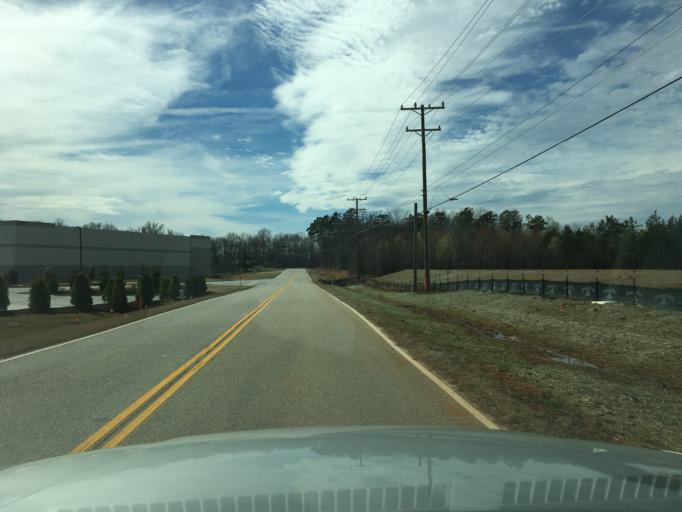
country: US
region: South Carolina
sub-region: Spartanburg County
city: Duncan
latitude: 34.9049
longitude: -82.1613
